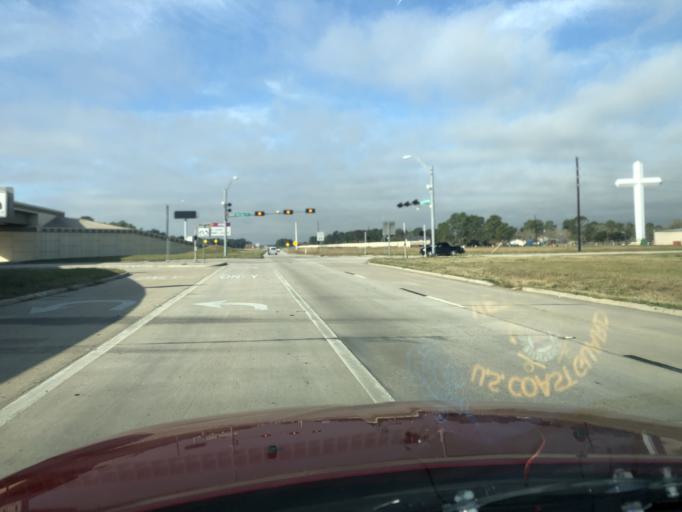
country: US
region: Texas
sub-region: Harris County
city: Tomball
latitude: 30.0522
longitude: -95.6198
